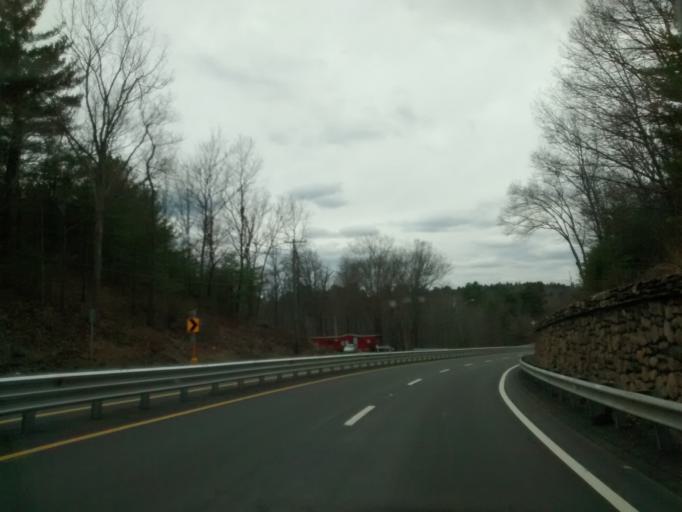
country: US
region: Massachusetts
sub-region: Worcester County
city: Oxford
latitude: 42.1556
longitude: -71.9052
